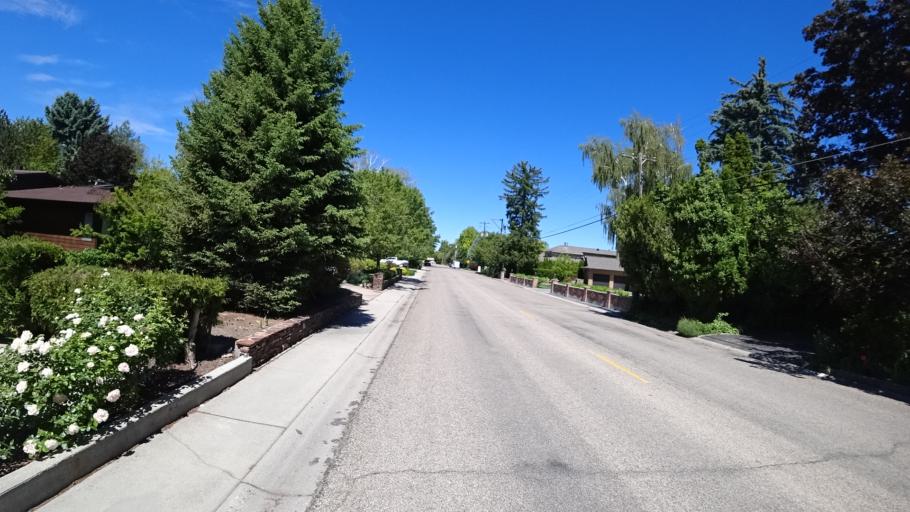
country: US
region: Idaho
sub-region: Ada County
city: Garden City
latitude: 43.5836
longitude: -116.2360
